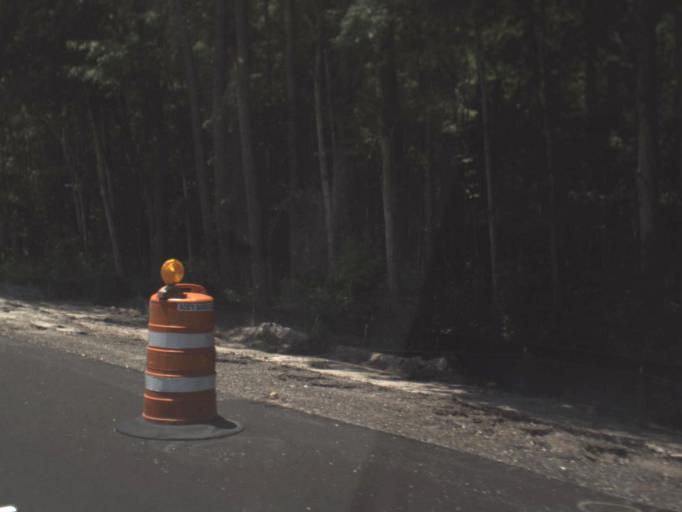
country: US
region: Florida
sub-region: Columbia County
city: Watertown
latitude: 30.2448
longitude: -82.5651
